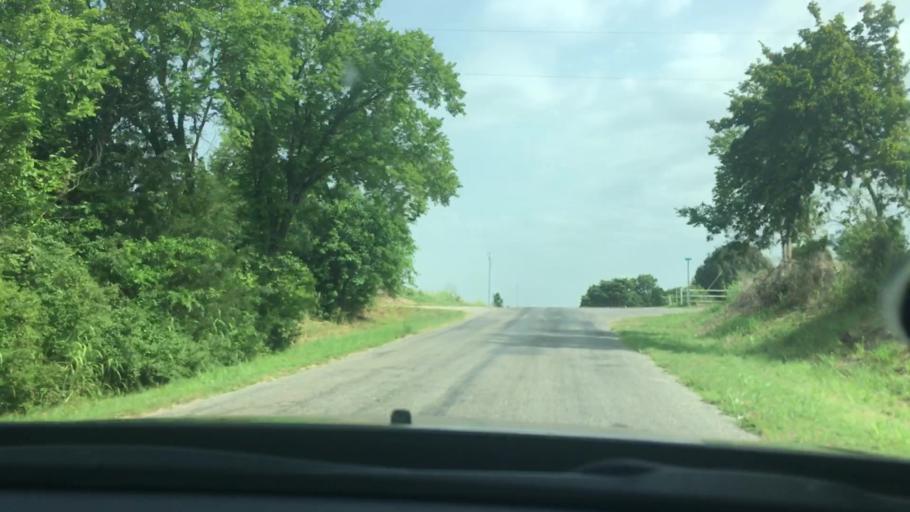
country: US
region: Oklahoma
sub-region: Garvin County
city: Pauls Valley
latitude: 34.8108
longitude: -97.1956
